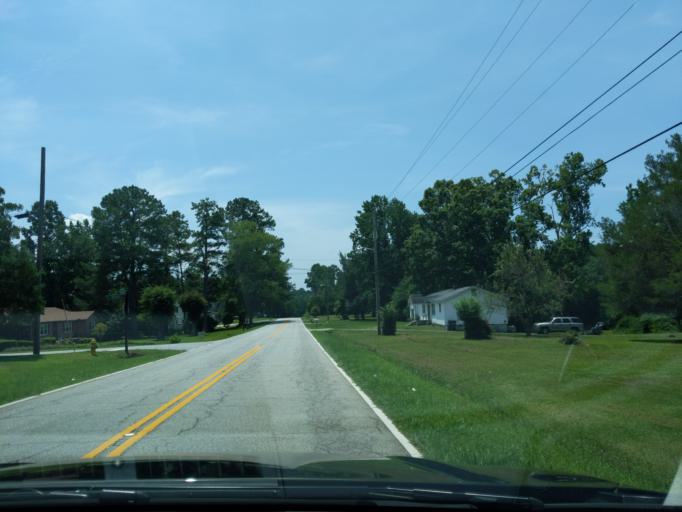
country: US
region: South Carolina
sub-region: Laurens County
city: Laurens
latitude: 34.4809
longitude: -82.0266
